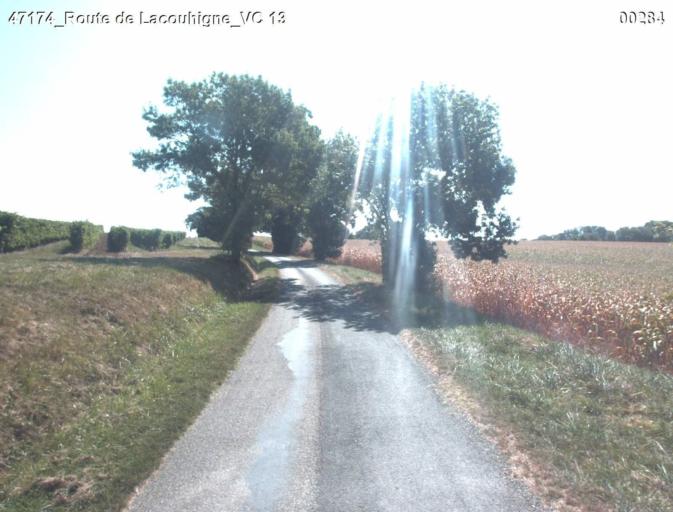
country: FR
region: Midi-Pyrenees
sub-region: Departement du Gers
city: Condom
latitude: 44.0184
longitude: 0.3888
